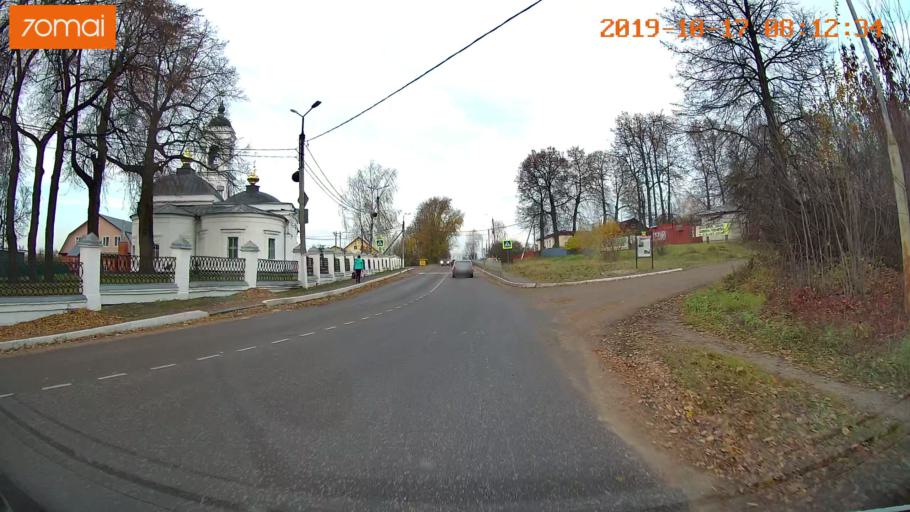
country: RU
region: Vladimir
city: Kol'chugino
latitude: 56.2993
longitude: 39.3565
